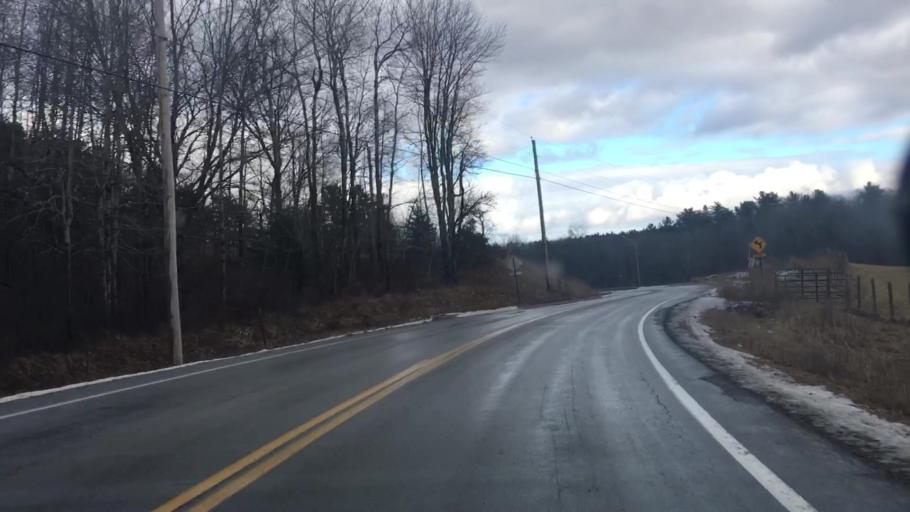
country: US
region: Maine
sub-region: Hancock County
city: Orland
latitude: 44.6300
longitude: -68.7051
